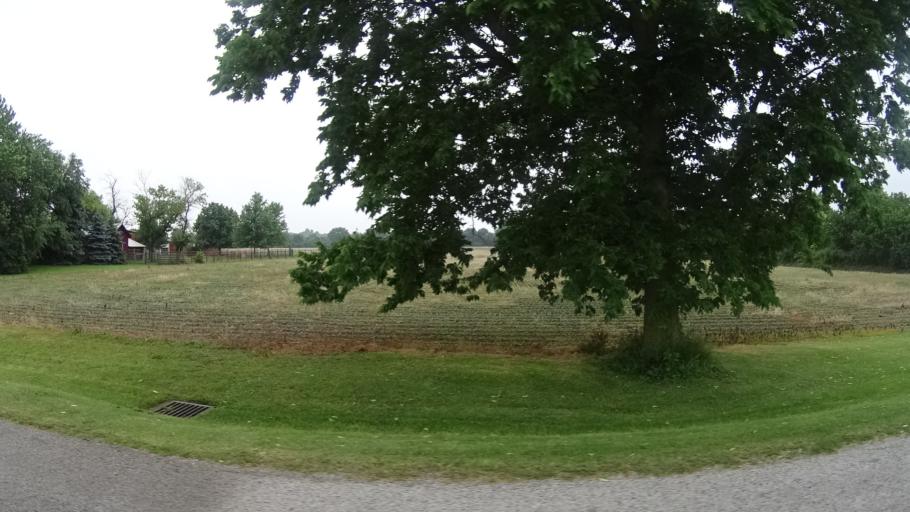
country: US
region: Ohio
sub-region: Huron County
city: Bellevue
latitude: 41.3562
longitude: -82.8171
